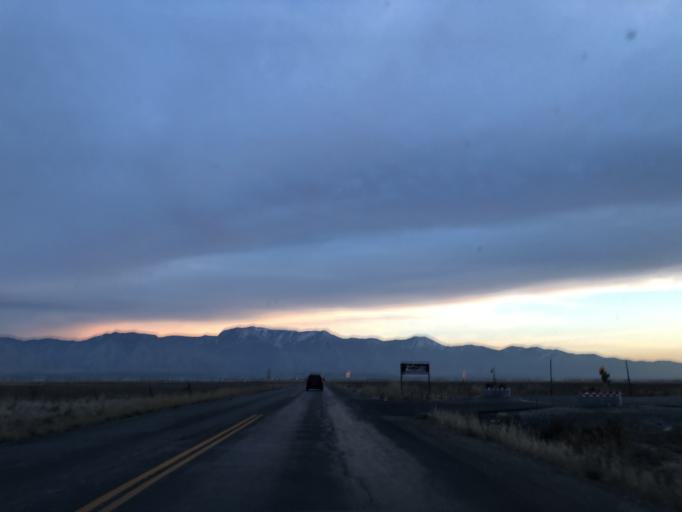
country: US
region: Utah
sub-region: Cache County
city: Benson
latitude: 41.7940
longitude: -111.8906
